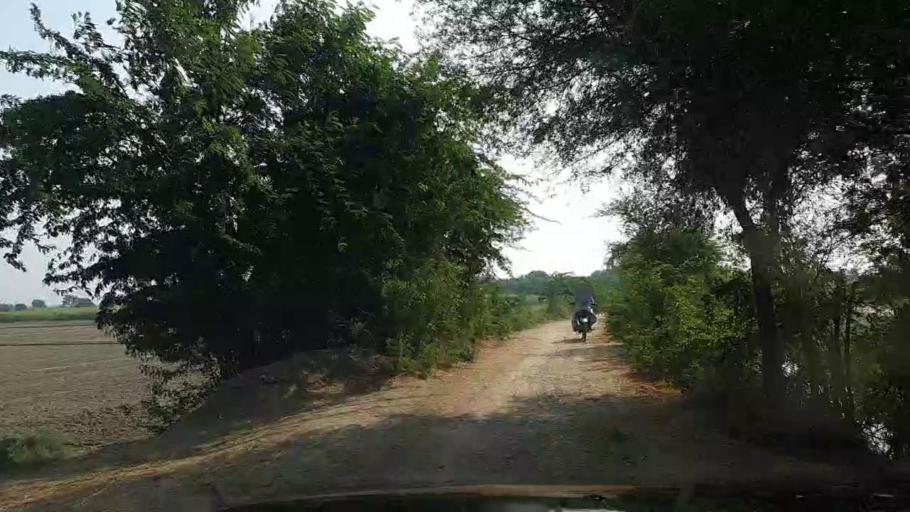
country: PK
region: Sindh
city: Mirpur Batoro
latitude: 24.6938
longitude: 68.2195
